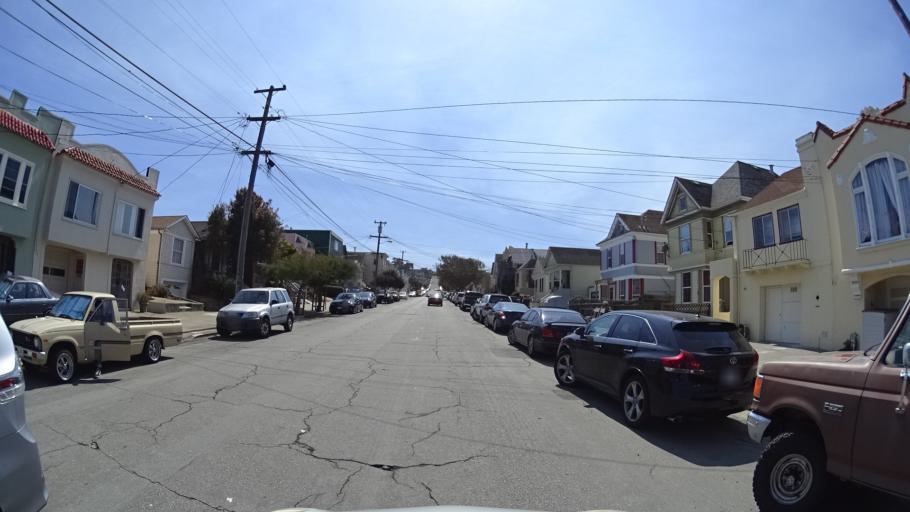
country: US
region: California
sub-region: San Mateo County
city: Daly City
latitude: 37.7232
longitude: -122.4582
